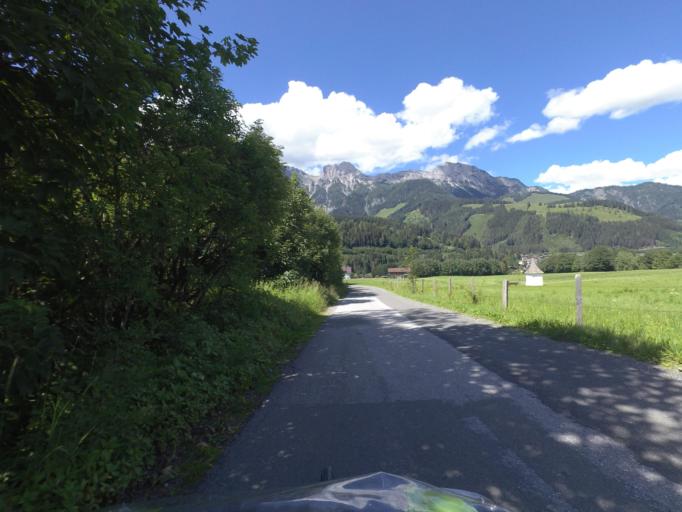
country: AT
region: Salzburg
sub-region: Politischer Bezirk Zell am See
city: Leogang
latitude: 47.4357
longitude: 12.7629
